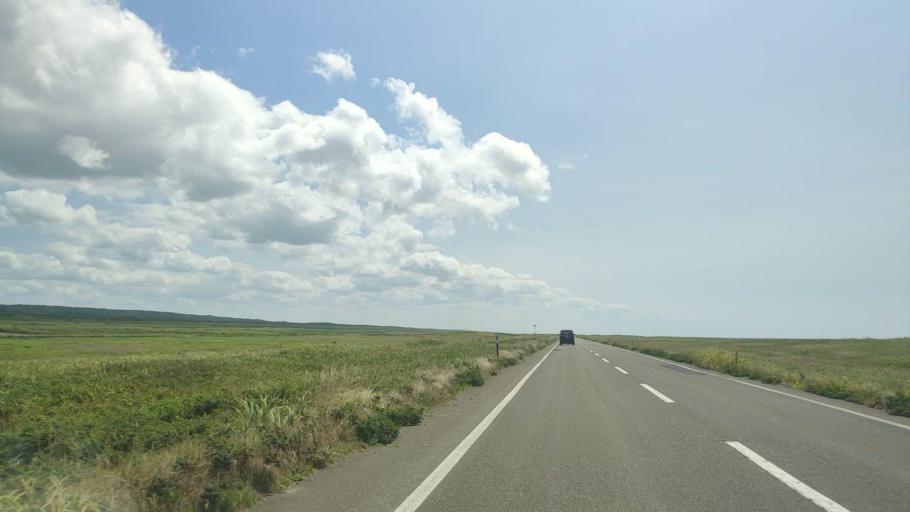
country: JP
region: Hokkaido
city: Wakkanai
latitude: 45.1188
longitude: 141.6103
